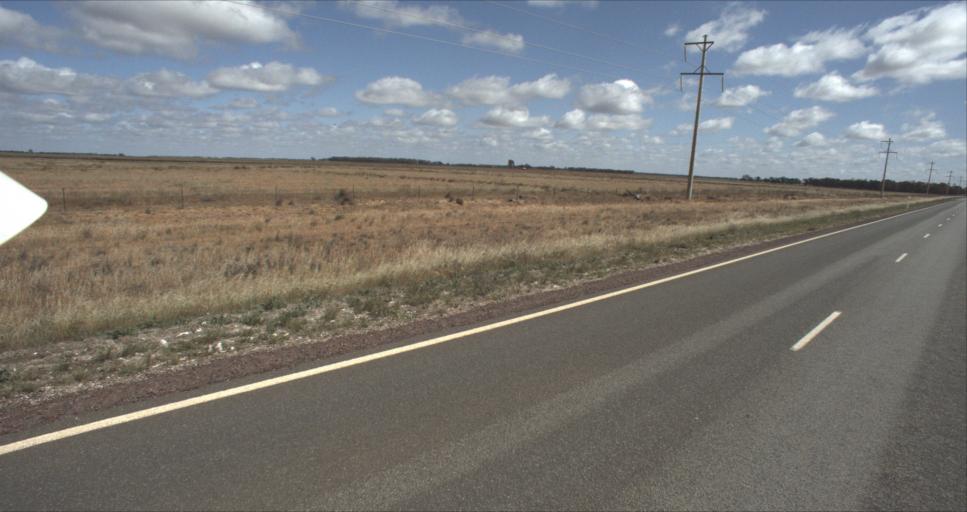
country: AU
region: New South Wales
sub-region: Murrumbidgee Shire
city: Darlington Point
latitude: -34.5850
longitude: 146.1644
